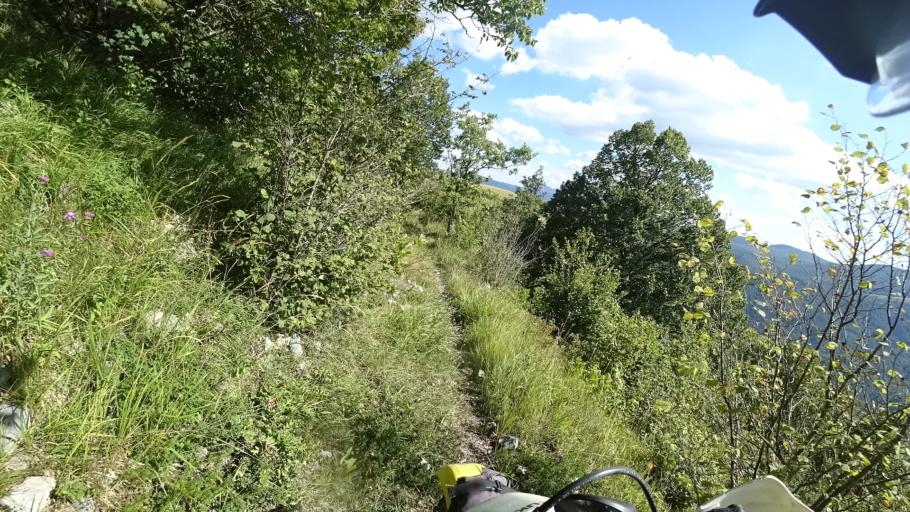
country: HR
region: Zadarska
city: Gracac
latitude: 44.3800
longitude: 16.0488
